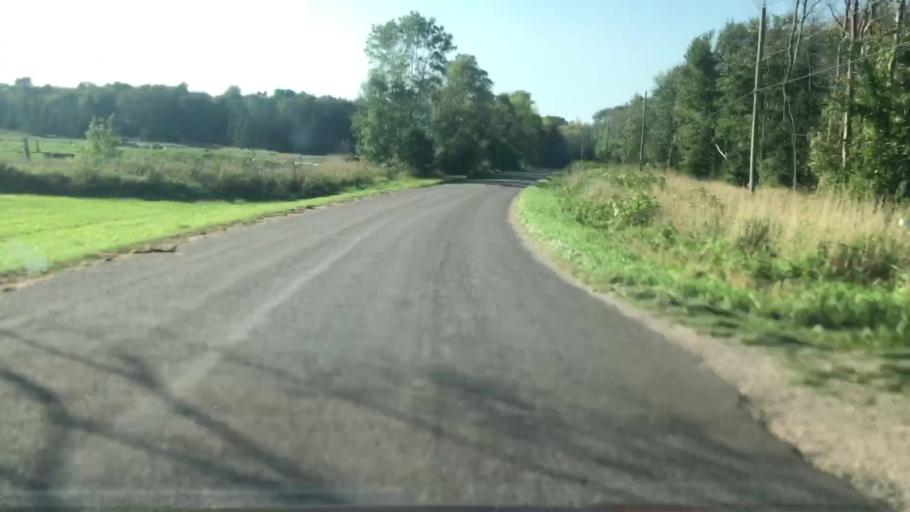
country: US
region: Michigan
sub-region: Chippewa County
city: Sault Ste. Marie
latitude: 46.2937
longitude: -84.0708
